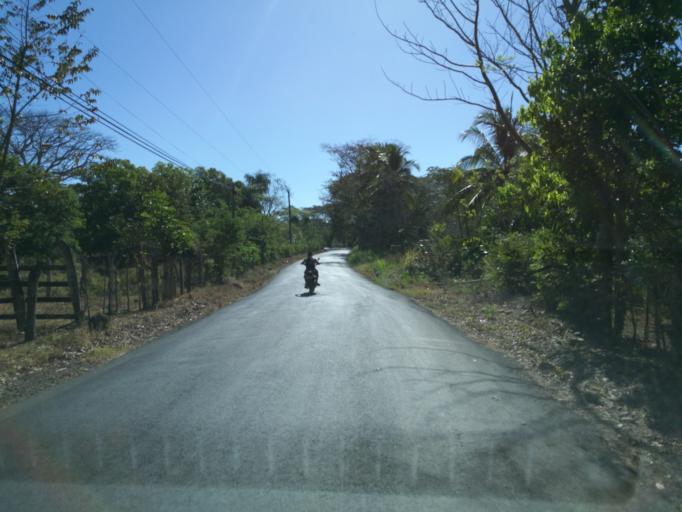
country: CR
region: Puntarenas
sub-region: Canton Central de Puntarenas
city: Puntarenas
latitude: 10.0910
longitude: -84.9599
